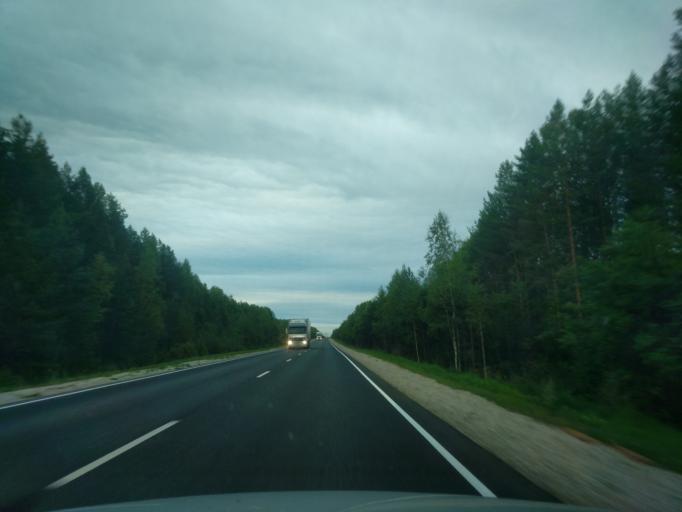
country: RU
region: Kostroma
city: Ponazyrevo
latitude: 58.3237
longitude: 46.5096
